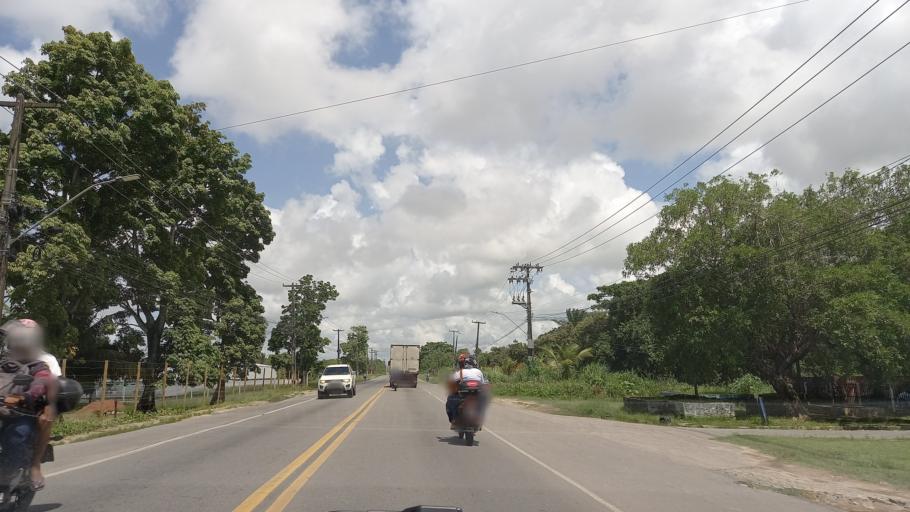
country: BR
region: Pernambuco
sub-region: Jaboatao Dos Guararapes
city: Jaboatao
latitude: -8.2269
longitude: -34.9697
